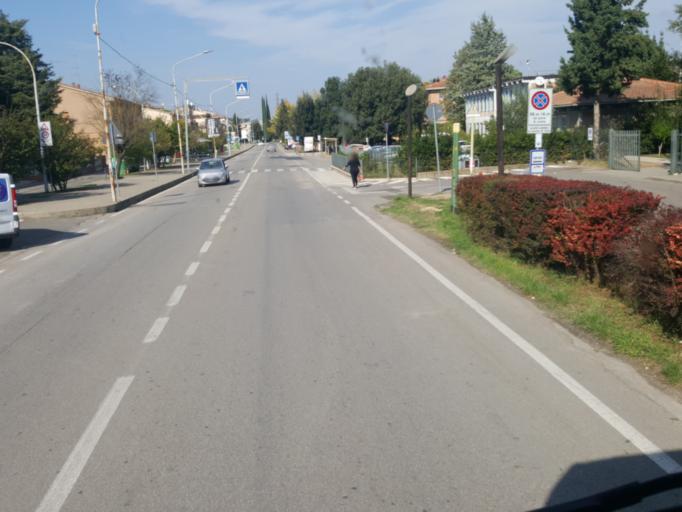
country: IT
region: Tuscany
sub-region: Provincia di Siena
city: Colle di Val d'Elsa
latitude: 43.4130
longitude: 11.1325
